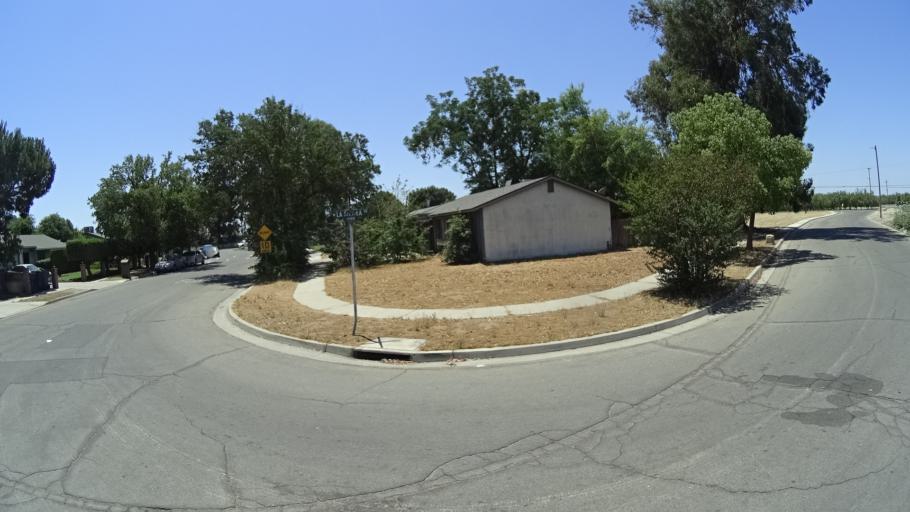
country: US
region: California
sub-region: Fresno County
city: West Park
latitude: 36.7308
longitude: -119.8343
